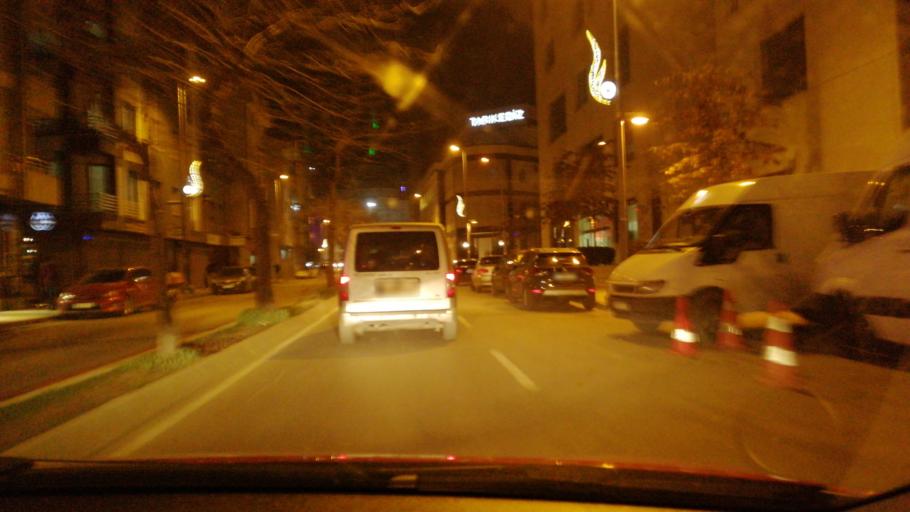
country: TR
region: Istanbul
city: Sisli
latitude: 41.0850
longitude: 28.9734
